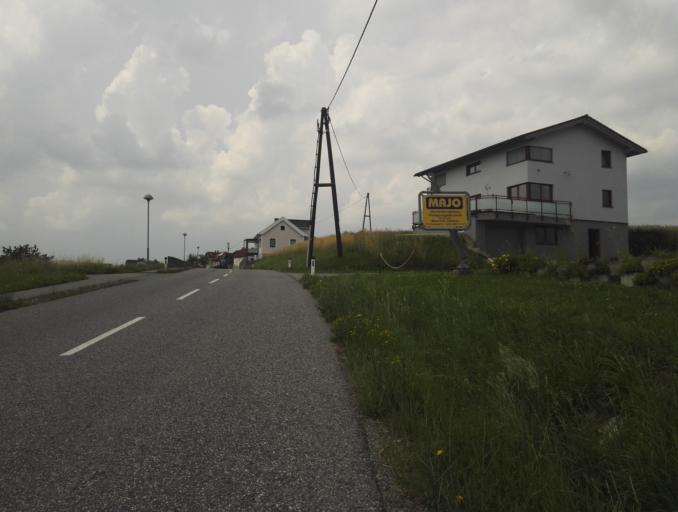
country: AT
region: Styria
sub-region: Politischer Bezirk Graz-Umgebung
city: Sankt Oswald bei Plankenwarth
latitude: 47.0890
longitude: 15.2854
